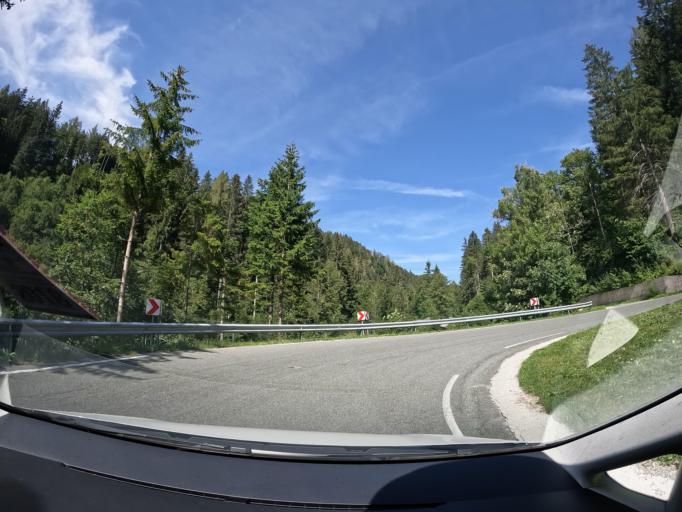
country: AT
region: Carinthia
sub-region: Politischer Bezirk Klagenfurt Land
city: Ludmannsdorf
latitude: 46.5044
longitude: 14.1002
